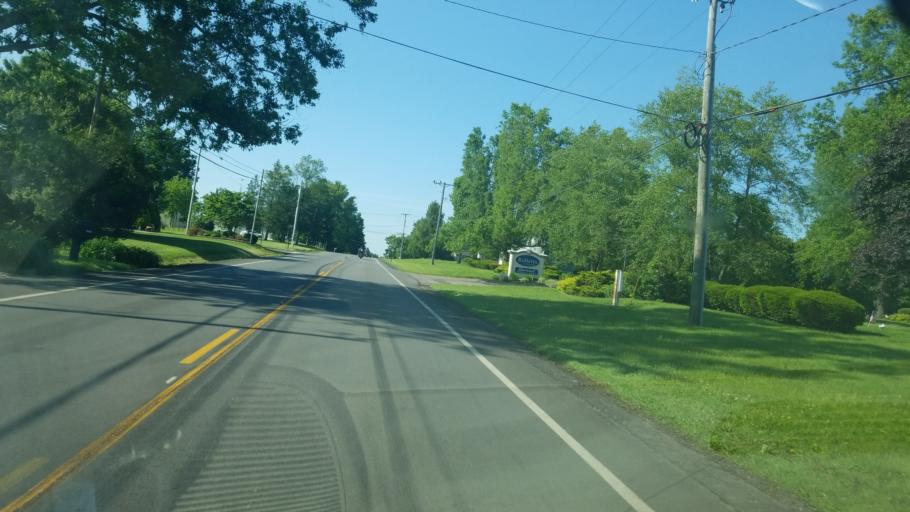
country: US
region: Ohio
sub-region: Wayne County
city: Smithville
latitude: 40.8848
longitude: -81.9186
